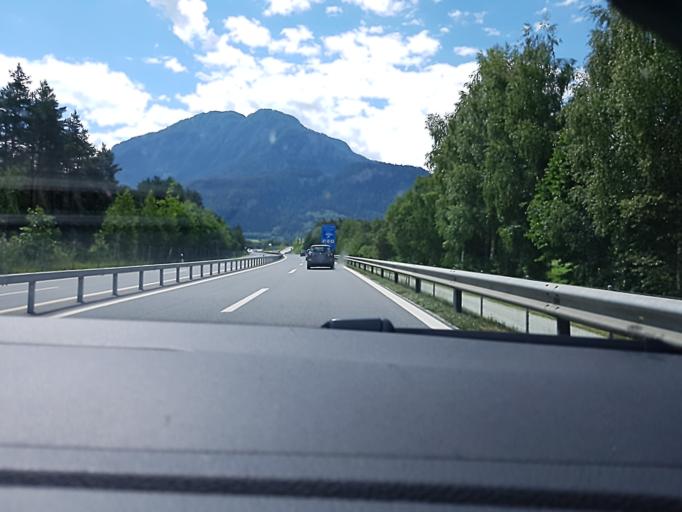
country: CH
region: Grisons
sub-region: Hinterrhein District
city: Cazis
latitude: 46.7190
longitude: 9.4414
